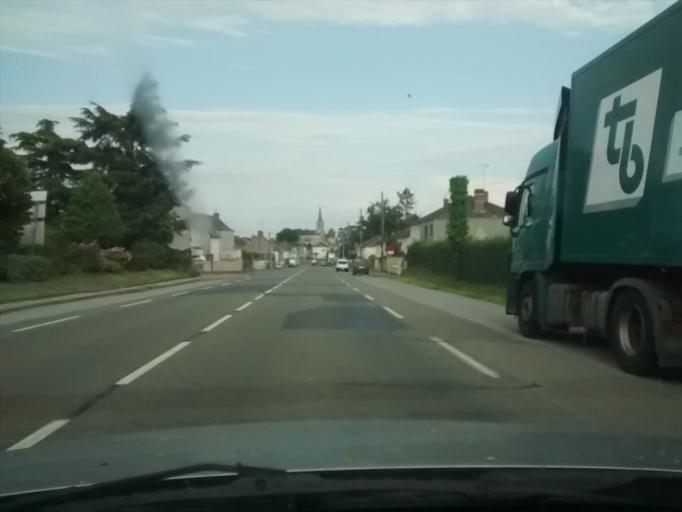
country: FR
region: Pays de la Loire
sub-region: Departement de la Mayenne
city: Soulge-sur-Ouette
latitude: 48.0605
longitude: -0.5748
